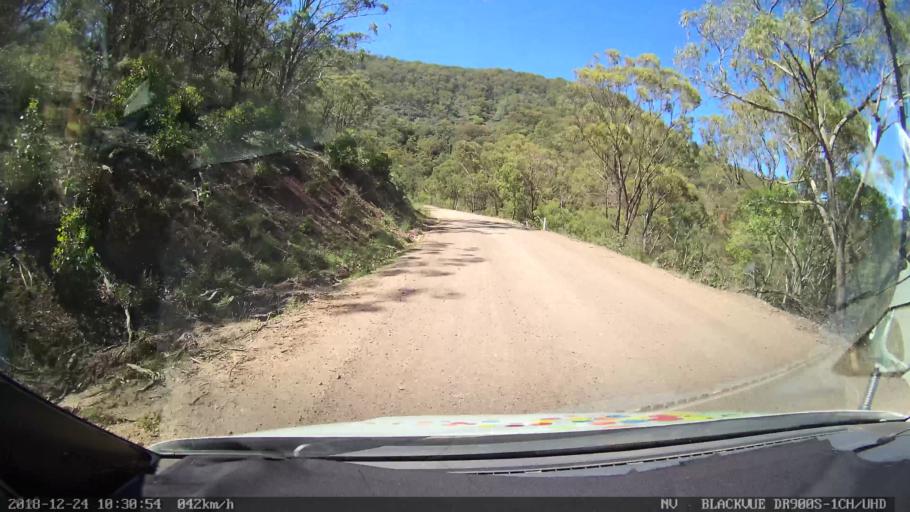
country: AU
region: New South Wales
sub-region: Upper Hunter Shire
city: Merriwa
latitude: -31.8369
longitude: 150.5233
